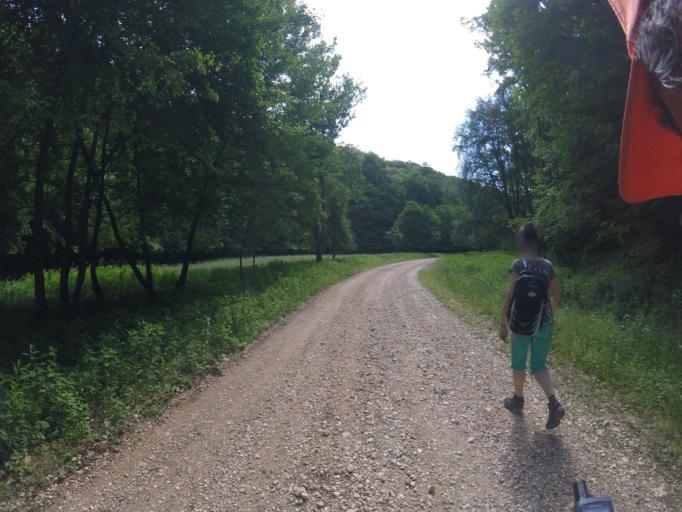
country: HU
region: Veszprem
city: Urkut
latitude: 47.1239
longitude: 17.6424
